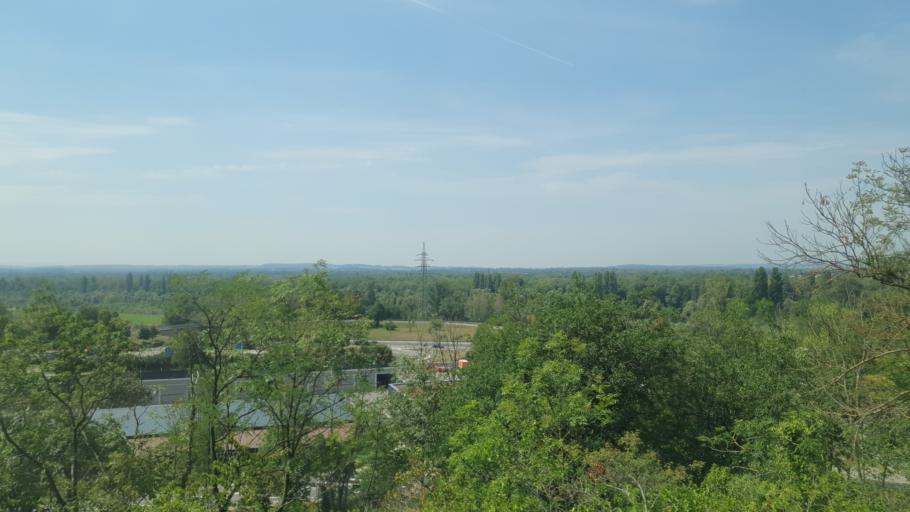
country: FR
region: Alsace
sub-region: Departement du Haut-Rhin
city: Kembs
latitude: 47.6797
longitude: 7.5268
